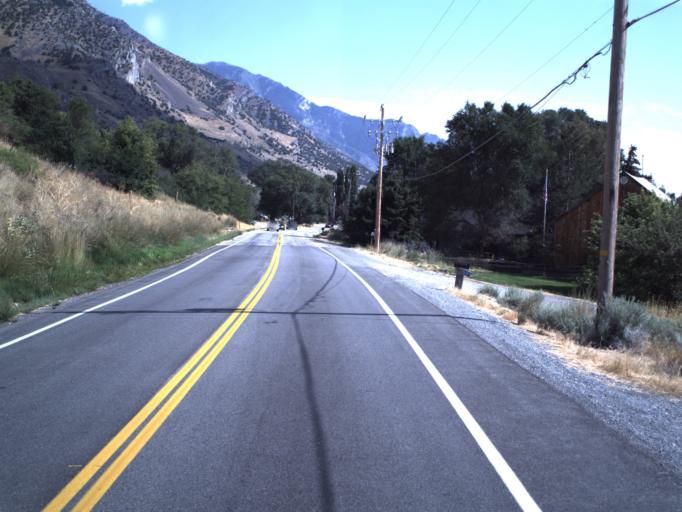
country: US
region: Utah
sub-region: Box Elder County
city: Elwood
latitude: 41.7129
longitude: -112.0921
